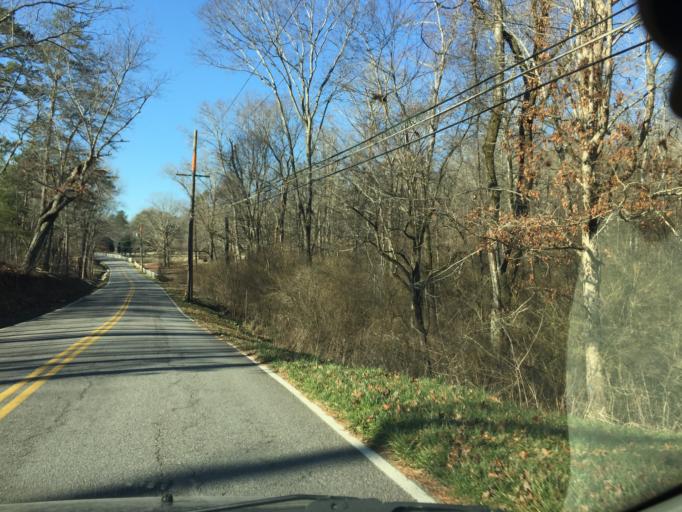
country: US
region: Tennessee
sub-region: Hamilton County
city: Collegedale
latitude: 35.0460
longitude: -85.0880
